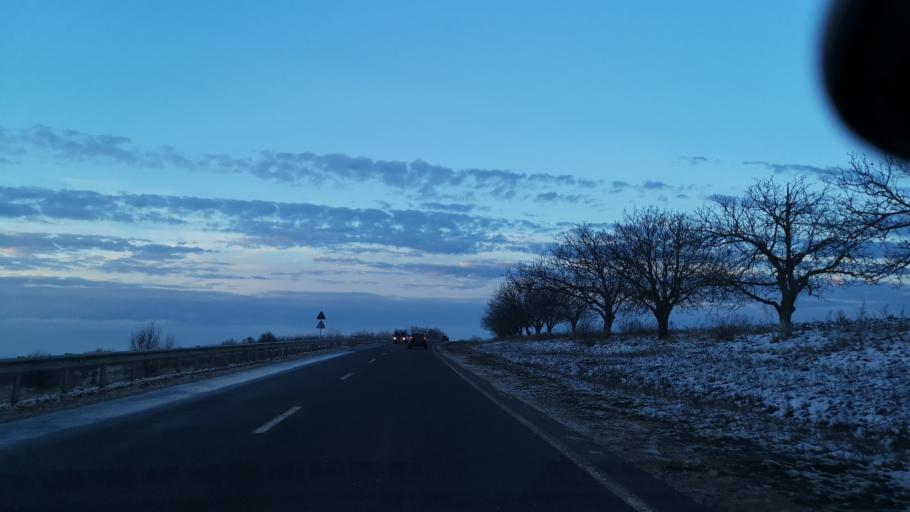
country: MD
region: Rezina
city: Saharna
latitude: 47.6062
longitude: 28.8308
